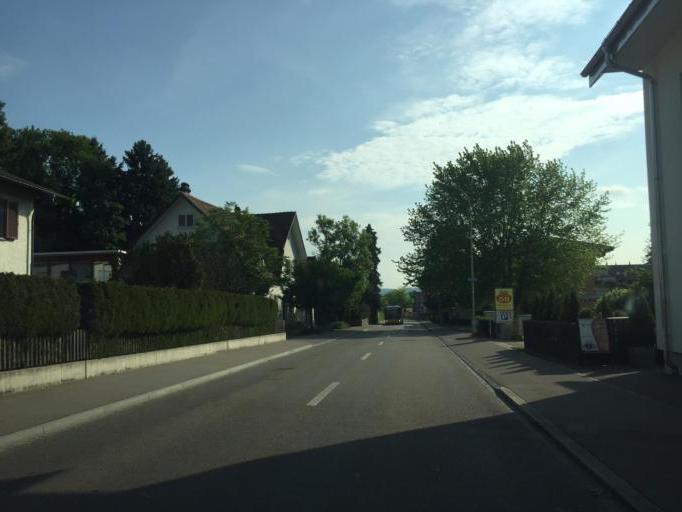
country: CH
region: Zurich
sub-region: Bezirk Dielsdorf
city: Oberglatt / Bahnhofquartier
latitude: 47.4710
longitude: 8.5115
